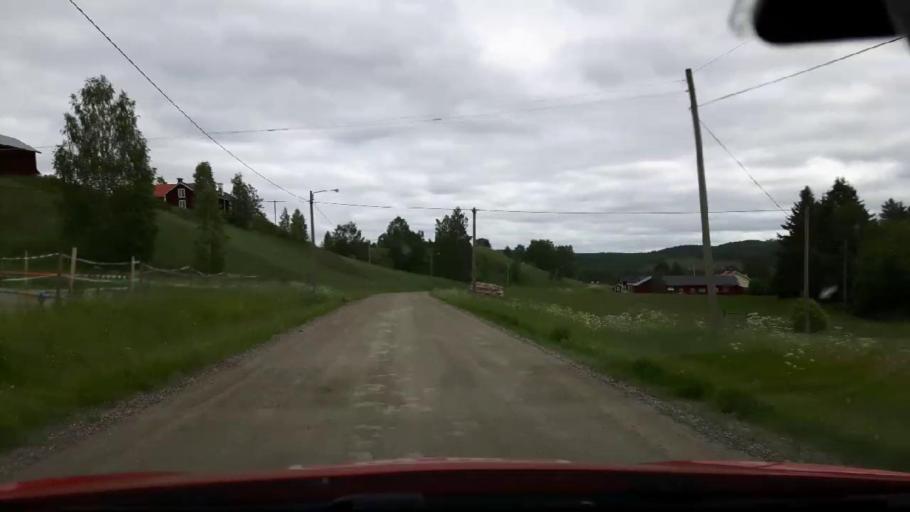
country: SE
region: Jaemtland
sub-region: Ragunda Kommun
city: Hammarstrand
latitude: 63.1647
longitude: 16.2168
